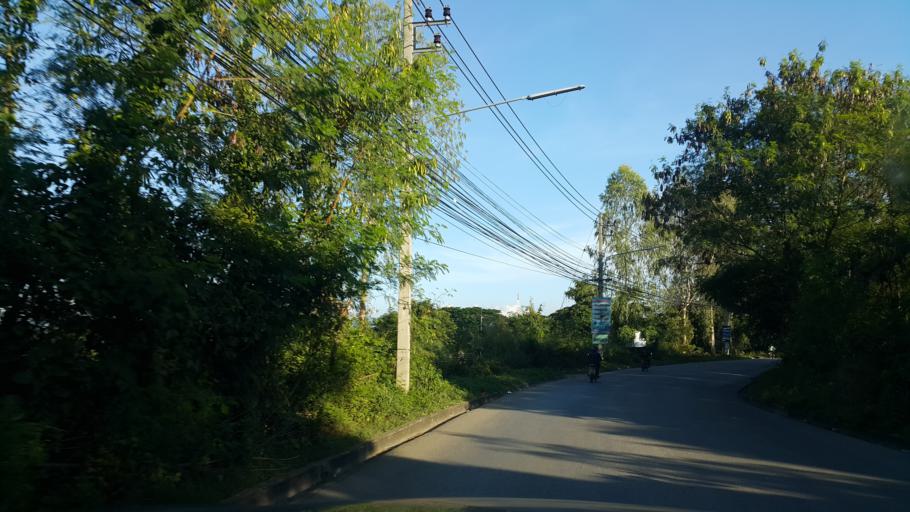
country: TH
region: Lamphun
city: Lamphun
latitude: 18.5970
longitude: 99.0316
